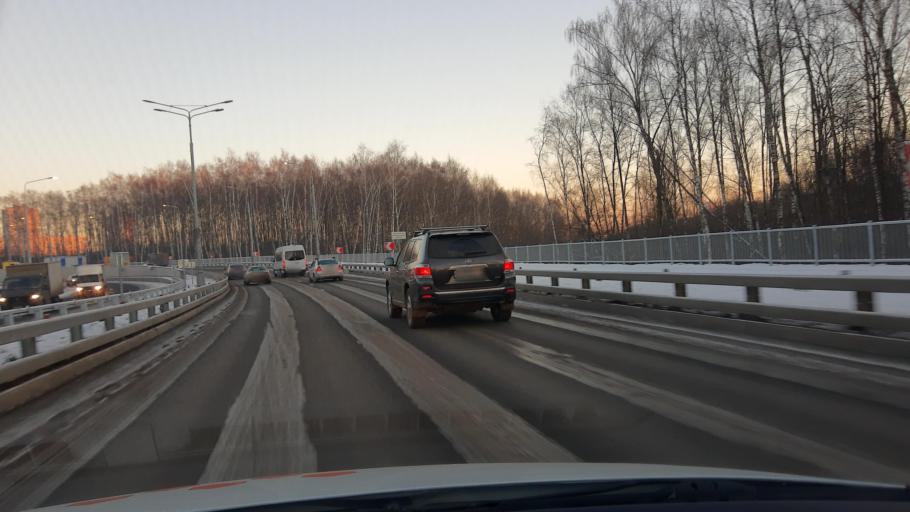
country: RU
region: Moscow
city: Tyoply Stan
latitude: 55.5997
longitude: 37.4976
